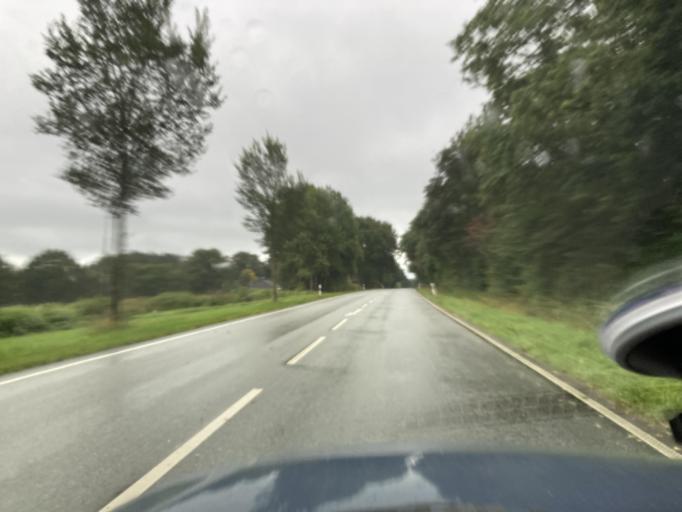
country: DE
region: Schleswig-Holstein
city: Gaushorn
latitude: 54.1961
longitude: 9.2160
